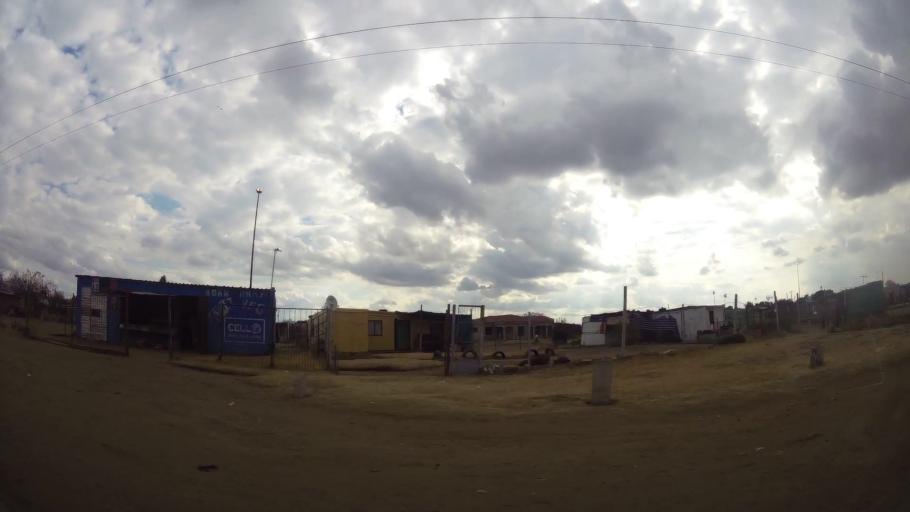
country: ZA
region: Orange Free State
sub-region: Fezile Dabi District Municipality
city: Sasolburg
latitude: -26.8551
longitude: 27.8529
